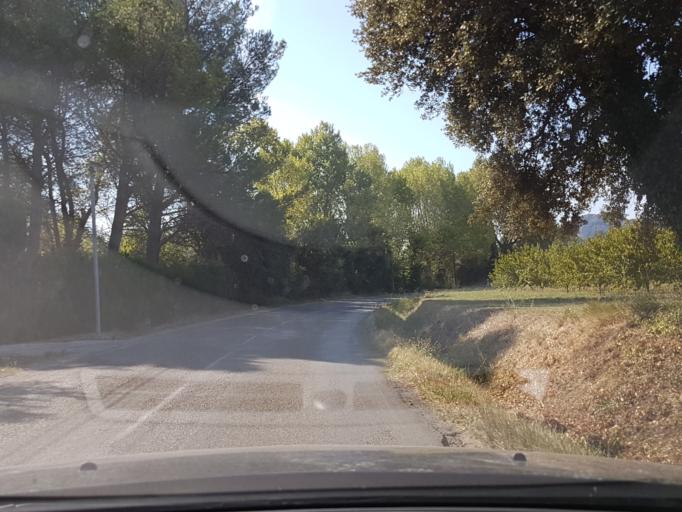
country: FR
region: Provence-Alpes-Cote d'Azur
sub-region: Departement des Bouches-du-Rhone
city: Eygalieres
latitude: 43.7715
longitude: 4.9303
